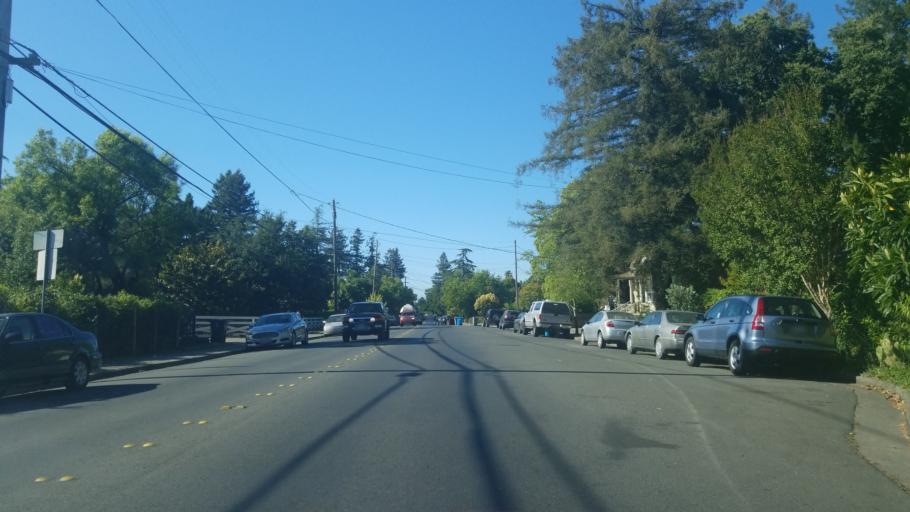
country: US
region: California
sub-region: Sonoma County
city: Roseland
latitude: 38.4262
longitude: -122.7248
